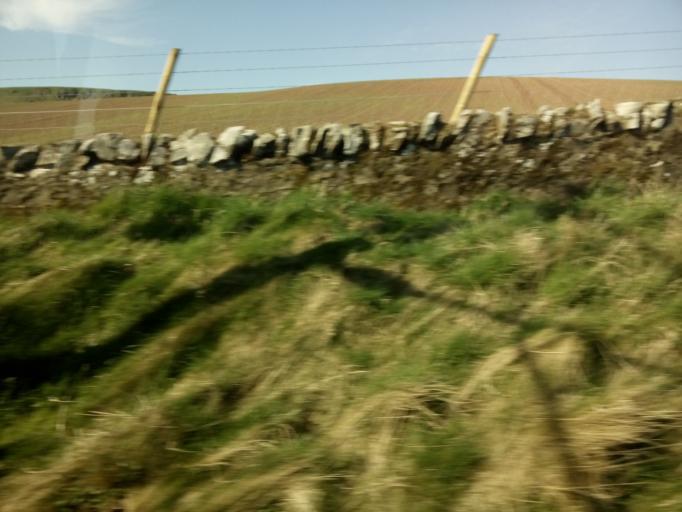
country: GB
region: Scotland
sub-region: The Scottish Borders
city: Eyemouth
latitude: 55.8406
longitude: -2.0706
